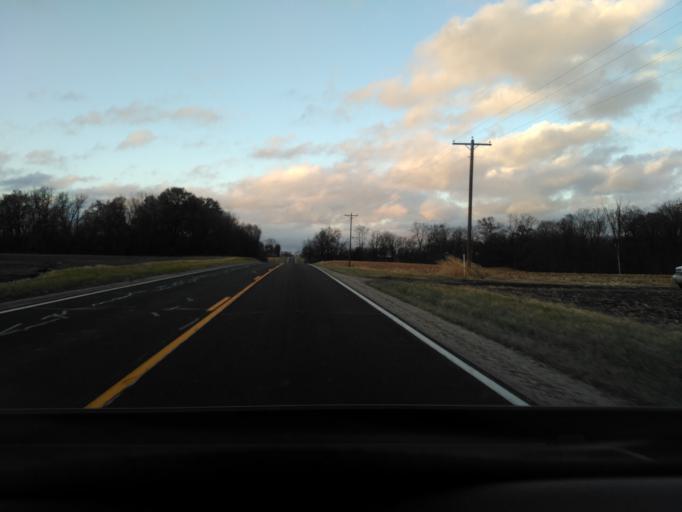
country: US
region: Illinois
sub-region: Effingham County
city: Altamont
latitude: 38.9788
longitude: -88.7489
